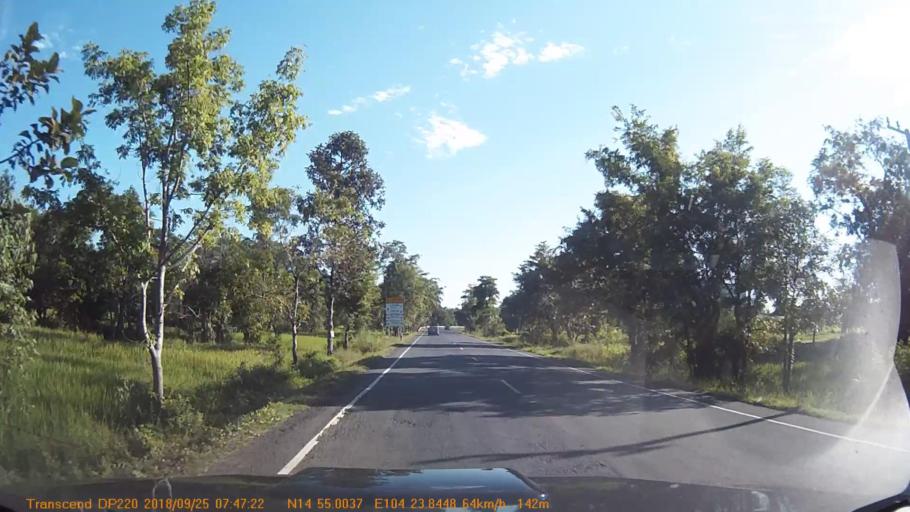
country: TH
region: Sisaket
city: Phayu
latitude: 14.9169
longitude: 104.3975
